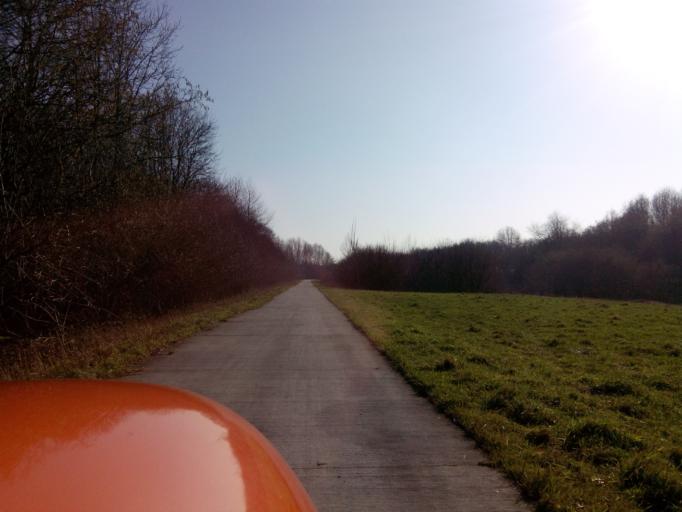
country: NL
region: Flevoland
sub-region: Gemeente Zeewolde
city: Zeewolde
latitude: 52.3280
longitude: 5.4813
